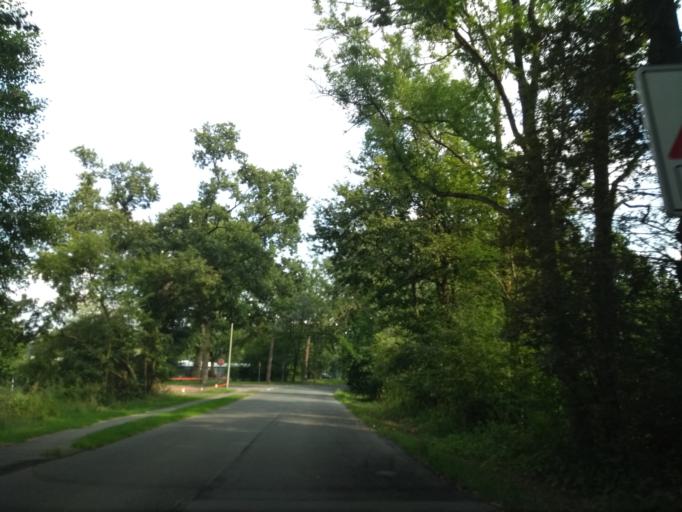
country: DE
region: North Rhine-Westphalia
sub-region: Regierungsbezirk Detmold
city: Paderborn
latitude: 51.7707
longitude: 8.7261
